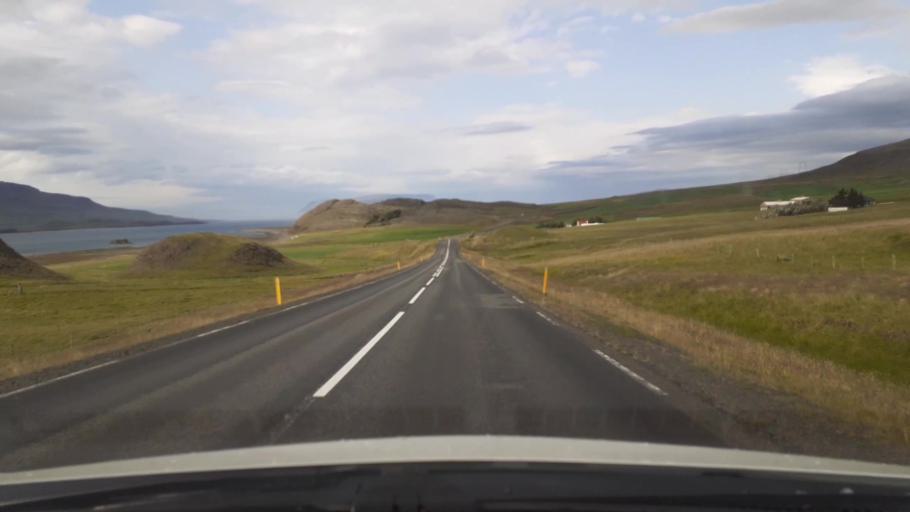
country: IS
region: Capital Region
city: Mosfellsbaer
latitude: 64.3986
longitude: -21.4991
